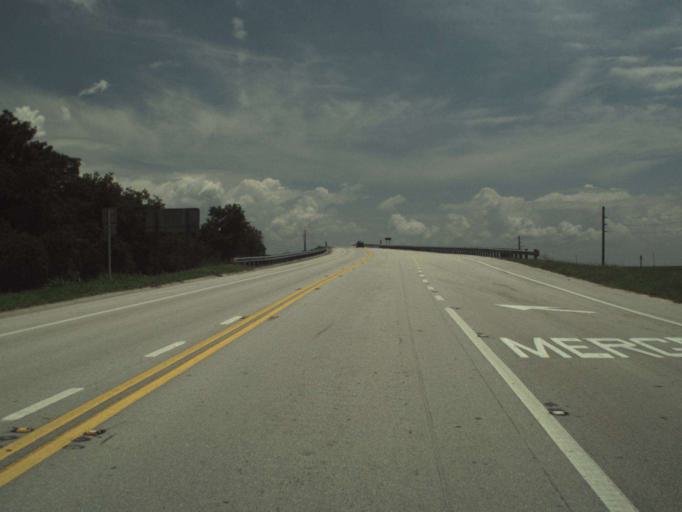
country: US
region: Florida
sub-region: Martin County
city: Indiantown
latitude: 26.9909
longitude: -80.6186
